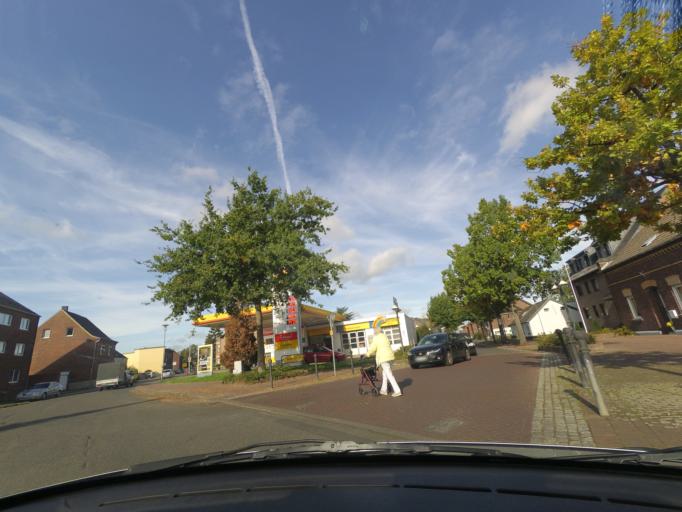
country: DE
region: North Rhine-Westphalia
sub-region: Regierungsbezirk Dusseldorf
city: Korschenbroich
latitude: 51.1920
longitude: 6.5560
